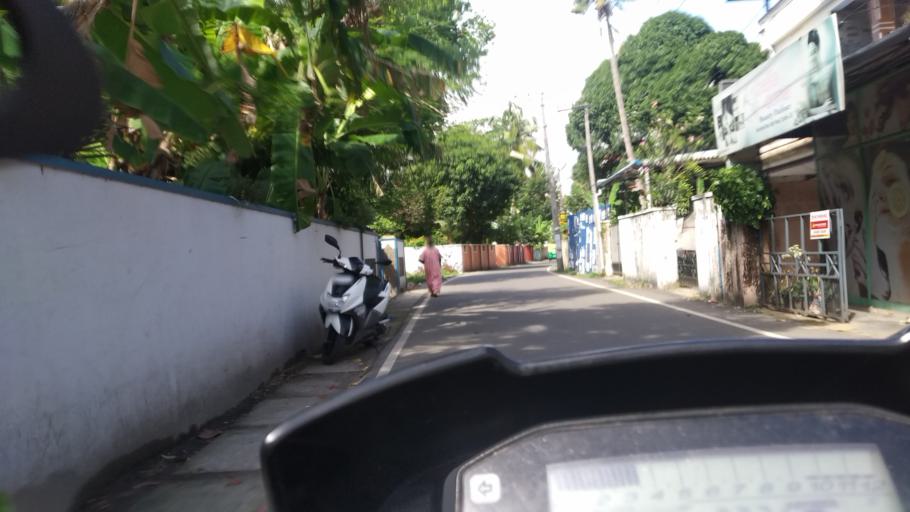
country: IN
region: Kerala
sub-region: Ernakulam
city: Elur
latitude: 10.0225
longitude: 76.2717
